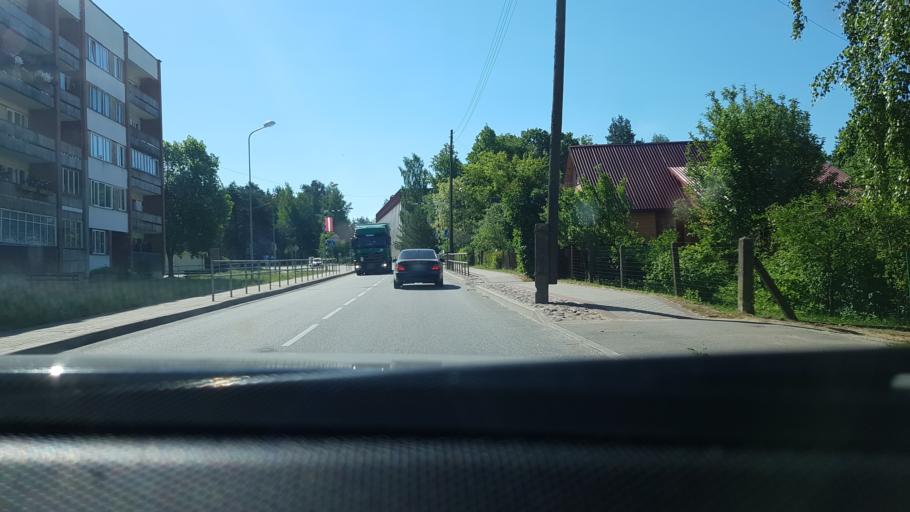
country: LV
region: Kraslavas Rajons
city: Kraslava
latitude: 55.8883
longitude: 27.1733
